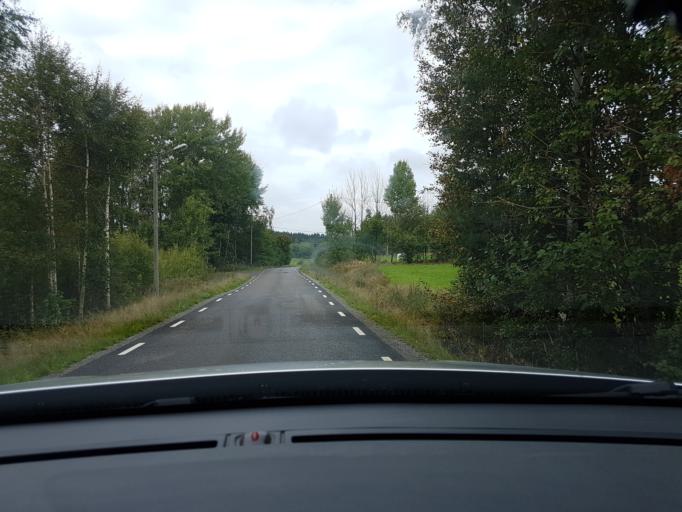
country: SE
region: Vaestra Goetaland
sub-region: Ale Kommun
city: Skepplanda
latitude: 57.8939
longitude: 12.1943
